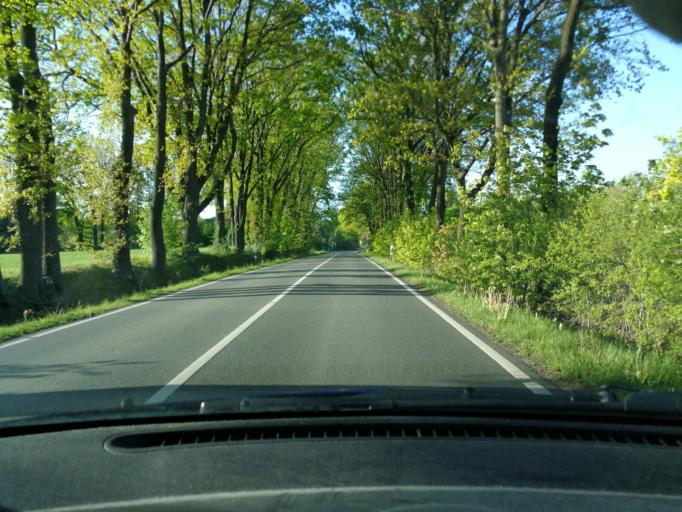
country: DE
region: Lower Saxony
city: Betzendorf
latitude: 53.1336
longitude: 10.3096
